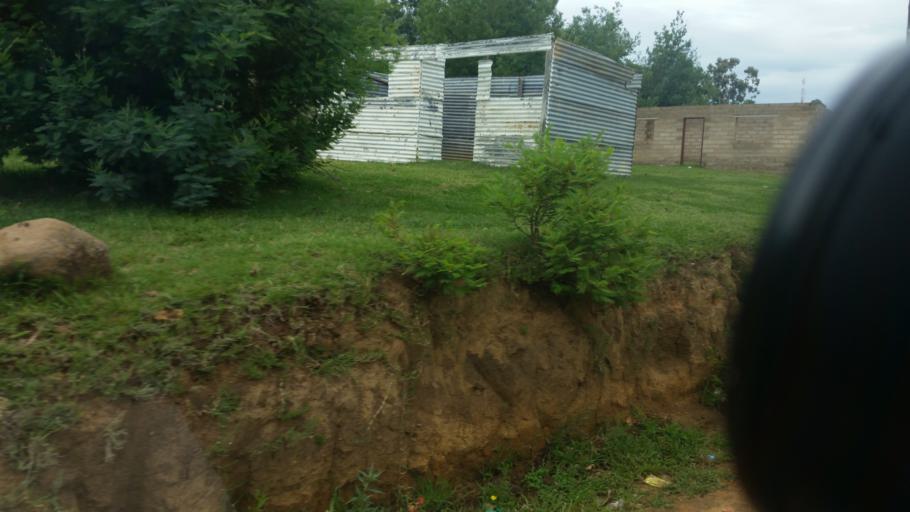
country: LS
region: Berea
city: Teyateyaneng
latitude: -29.1144
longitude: 27.9666
